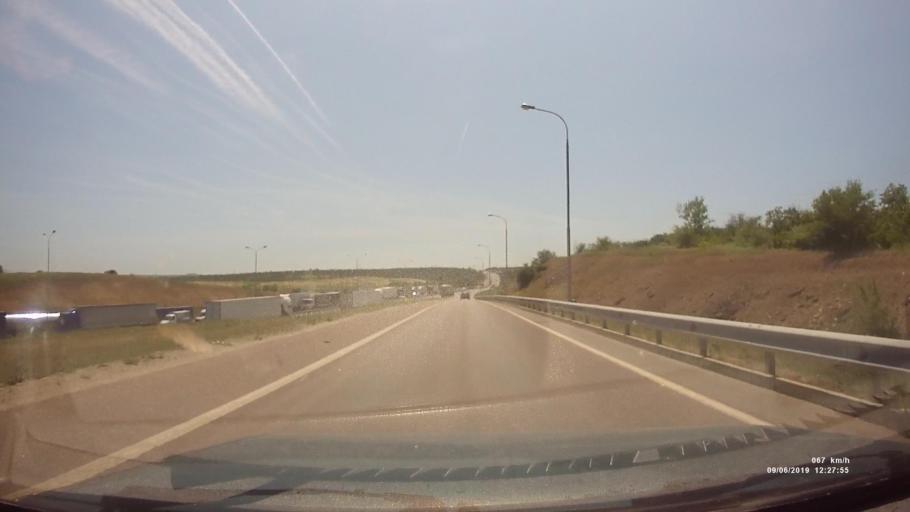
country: RU
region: Rostov
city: Staraya Stanitsa
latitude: 48.2966
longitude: 40.2965
